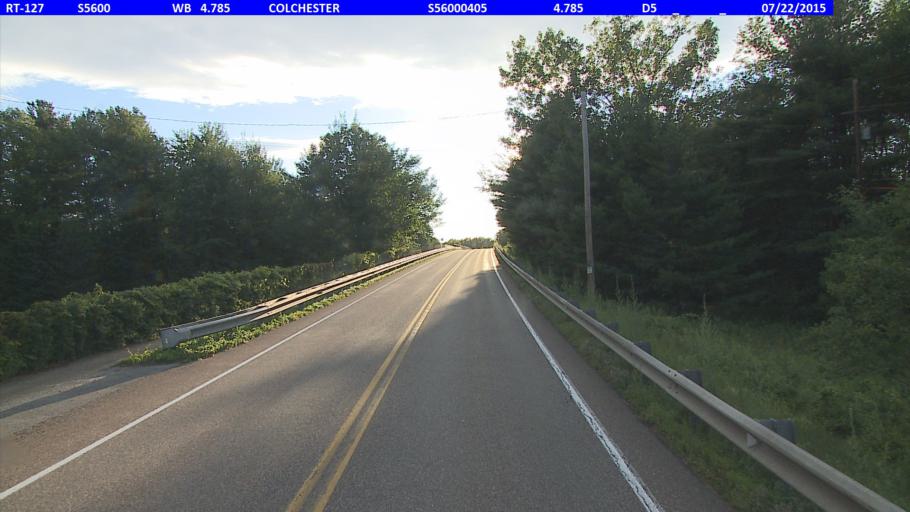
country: US
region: Vermont
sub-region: Chittenden County
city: Winooski
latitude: 44.5300
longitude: -73.1929
